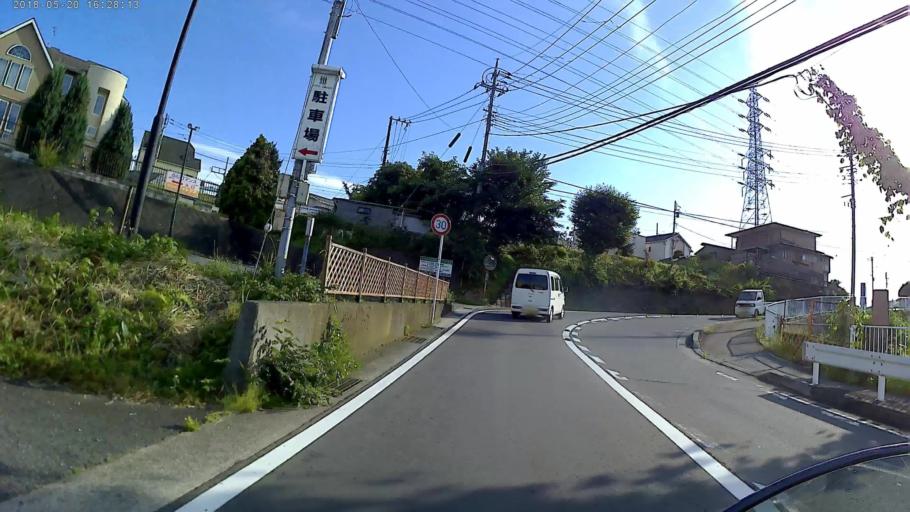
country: JP
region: Kanagawa
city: Odawara
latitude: 35.2757
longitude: 139.1526
